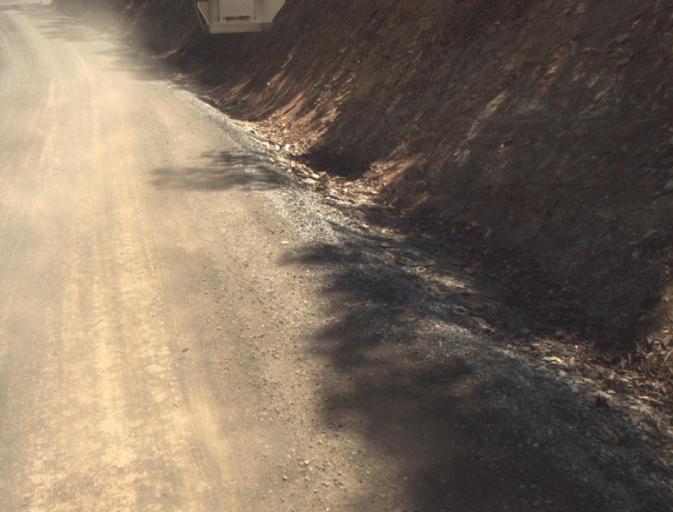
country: AU
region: Tasmania
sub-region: Dorset
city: Scottsdale
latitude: -41.2940
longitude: 147.3407
